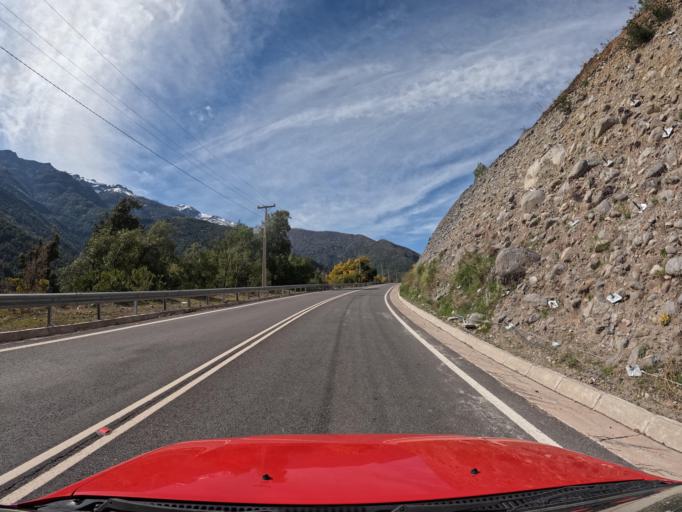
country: CL
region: O'Higgins
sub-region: Provincia de Colchagua
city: Chimbarongo
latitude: -34.9989
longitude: -70.8209
